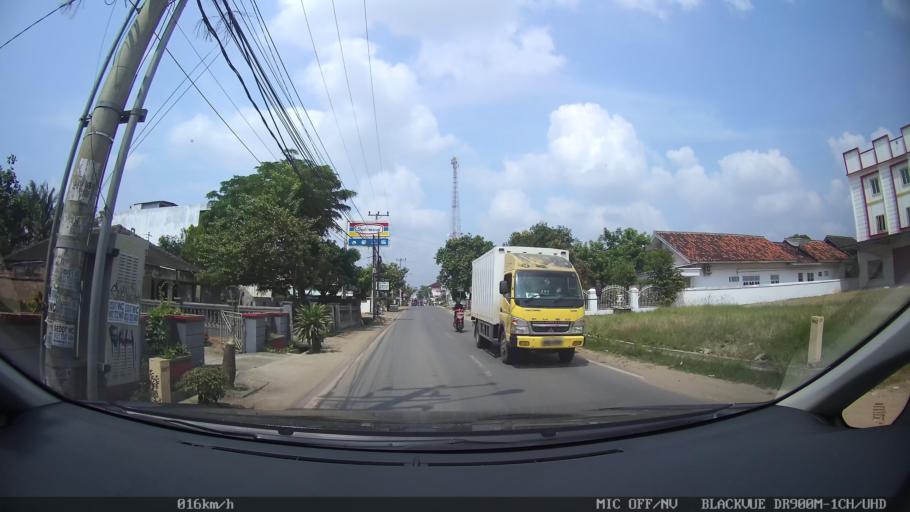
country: ID
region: Lampung
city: Pringsewu
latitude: -5.3623
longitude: 104.9763
